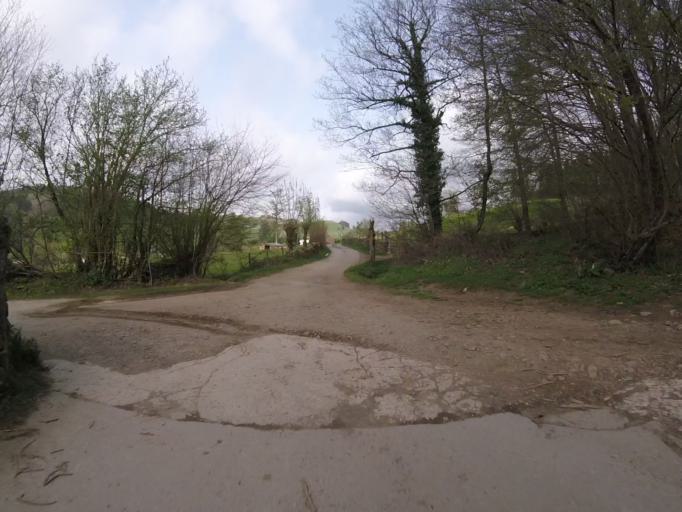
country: ES
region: Basque Country
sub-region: Provincia de Guipuzcoa
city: Berastegui
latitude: 43.1110
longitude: -1.9604
